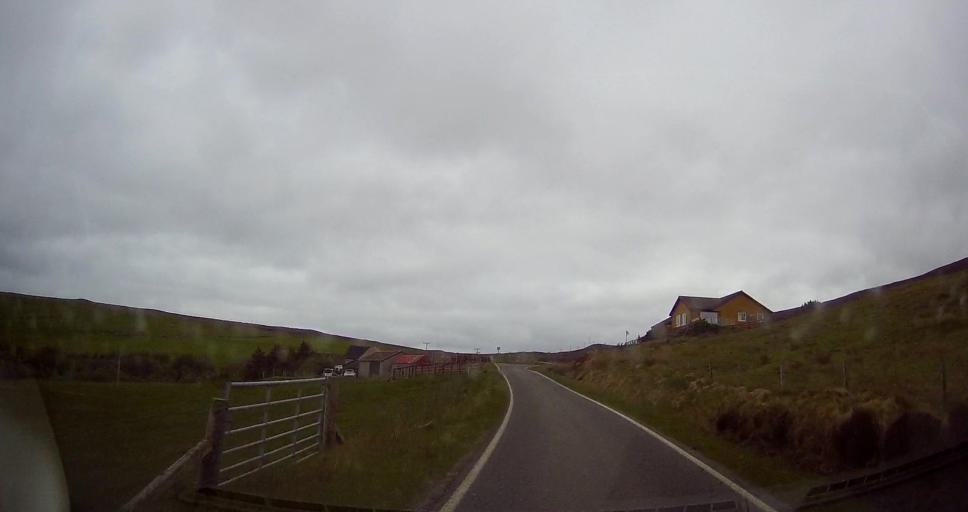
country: GB
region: Scotland
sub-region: Shetland Islands
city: Lerwick
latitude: 60.3049
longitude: -1.3381
